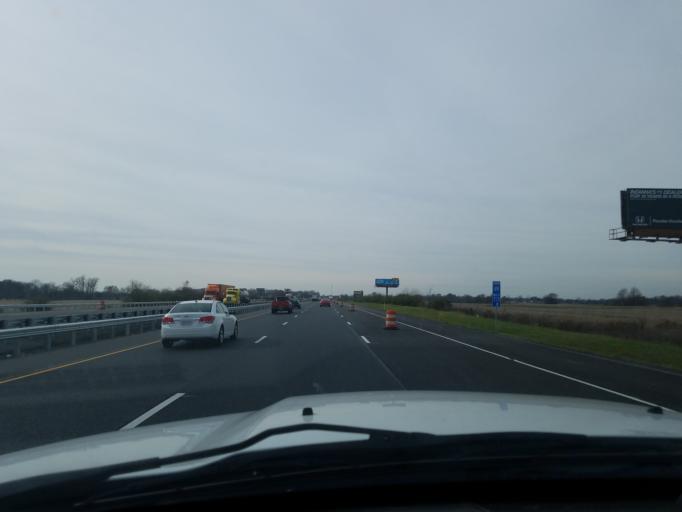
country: US
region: Indiana
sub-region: Hancock County
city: Fortville
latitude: 39.9930
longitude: -85.8551
